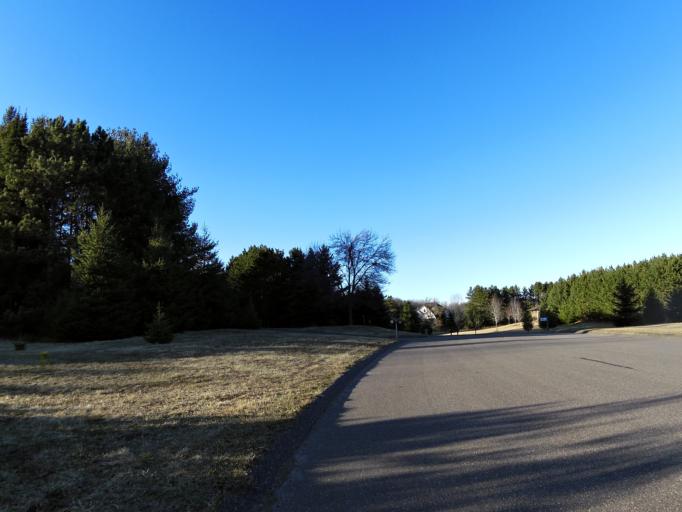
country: US
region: Minnesota
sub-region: Washington County
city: Lake Elmo
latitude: 44.9803
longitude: -92.8365
